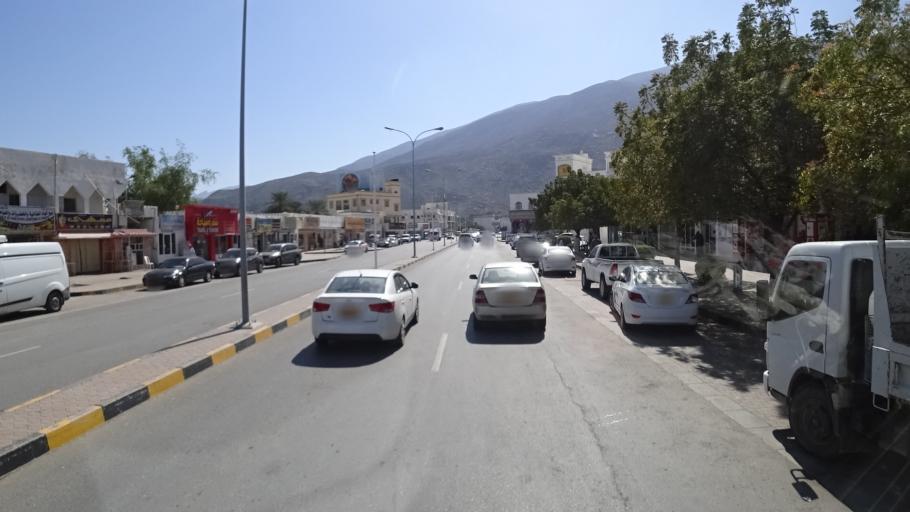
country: OM
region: Al Batinah
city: Rustaq
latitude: 23.3934
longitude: 57.4226
